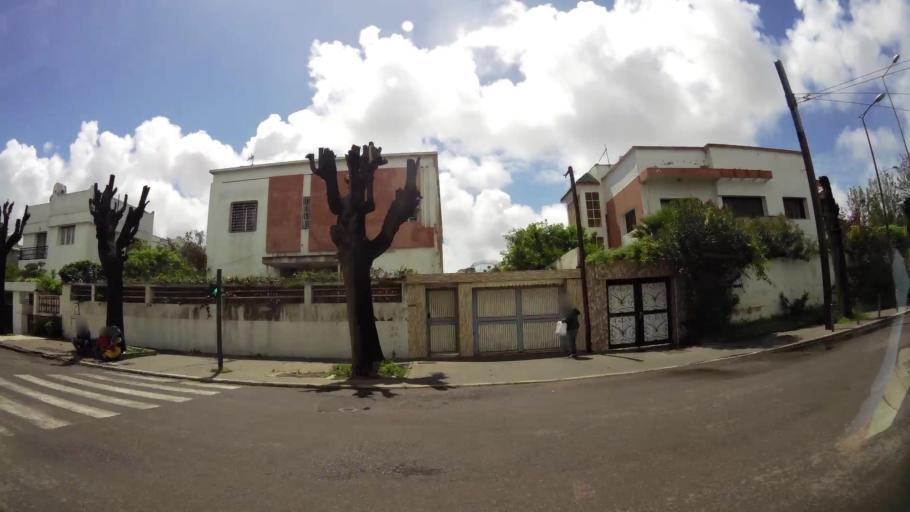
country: MA
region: Grand Casablanca
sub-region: Casablanca
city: Casablanca
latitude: 33.5694
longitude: -7.6402
